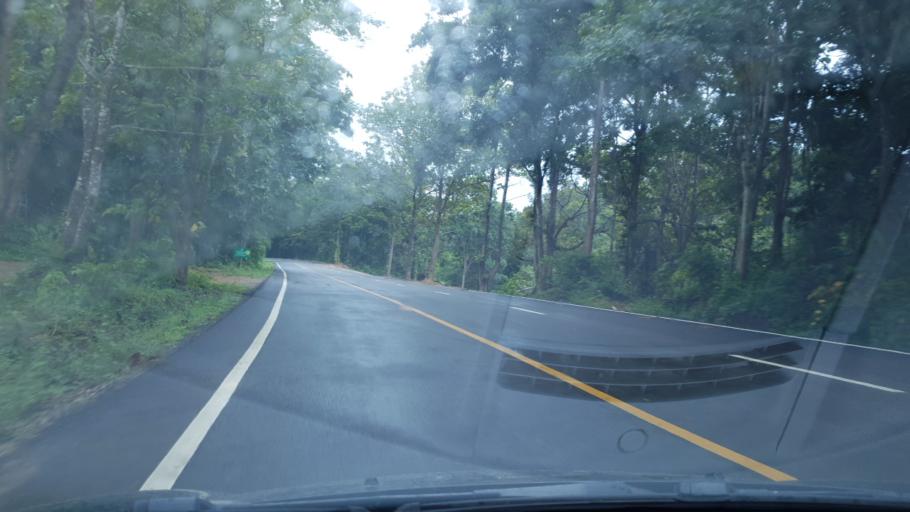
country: TH
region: Mae Hong Son
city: Pa Pae
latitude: 18.2608
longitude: 97.9420
